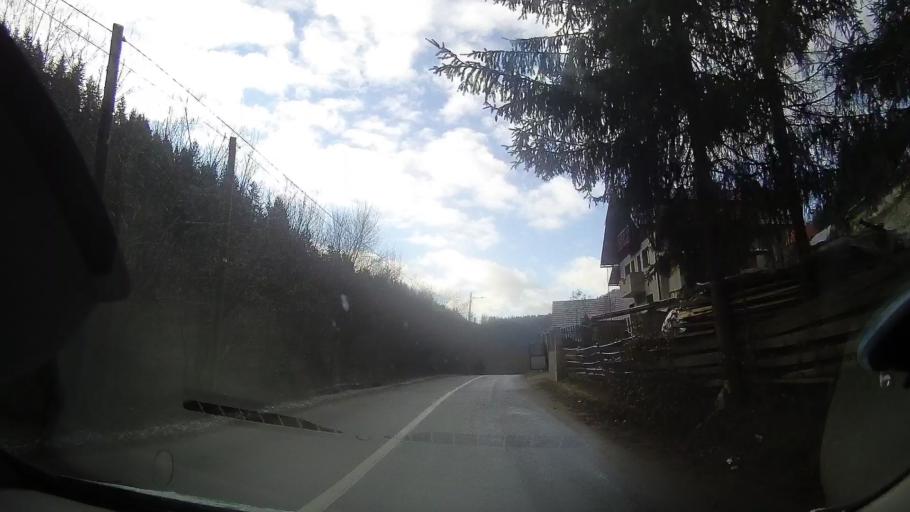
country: RO
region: Alba
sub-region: Comuna Albac
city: Albac
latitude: 46.4548
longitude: 22.9739
